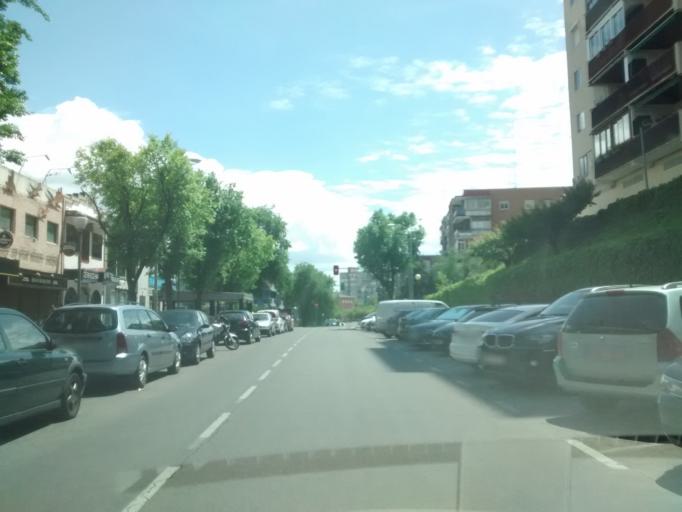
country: ES
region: Madrid
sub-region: Provincia de Madrid
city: San Fernando de Henares
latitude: 40.4260
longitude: -3.5398
